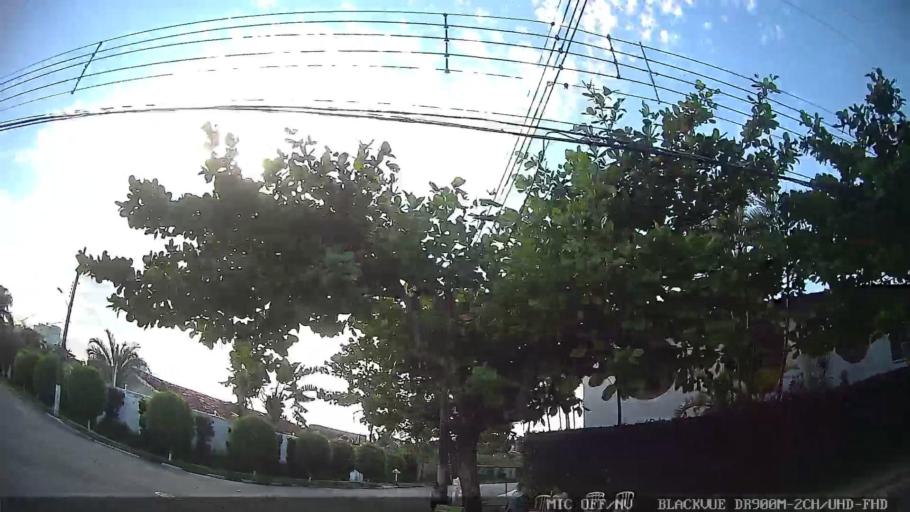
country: BR
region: Sao Paulo
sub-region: Guaruja
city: Guaruja
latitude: -23.9848
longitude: -46.2244
